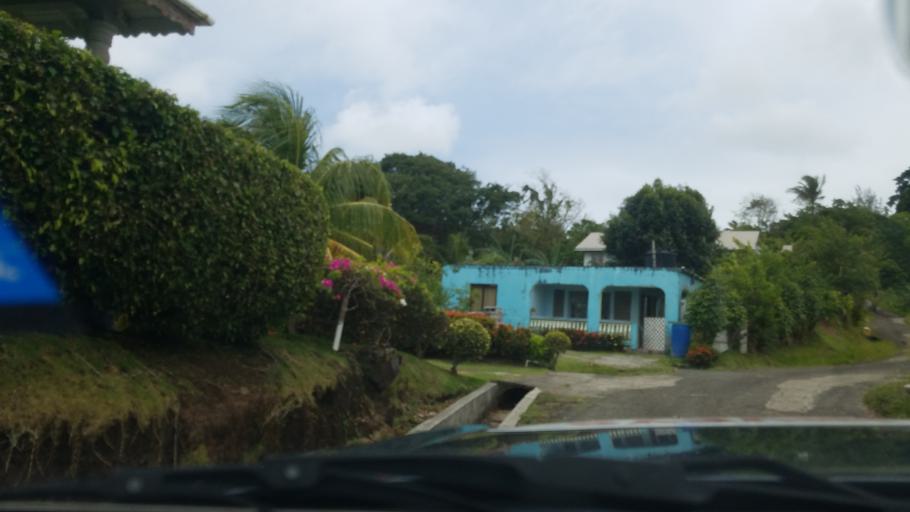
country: LC
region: Castries Quarter
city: Bisee
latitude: 14.0155
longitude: -60.9235
